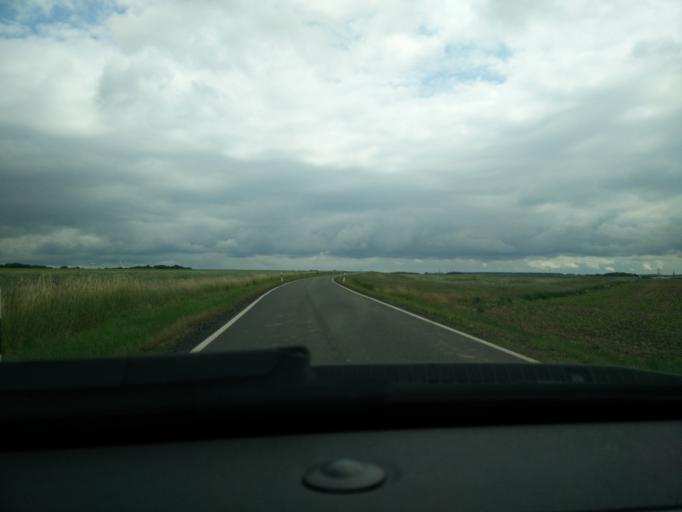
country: DE
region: Saxony
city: Bad Lausick
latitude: 51.1129
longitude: 12.6601
